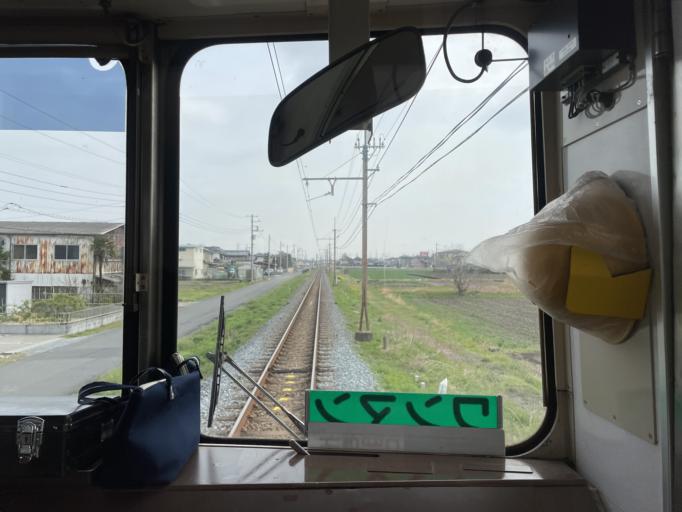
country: JP
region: Saitama
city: Kumagaya
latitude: 36.1361
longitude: 139.4037
